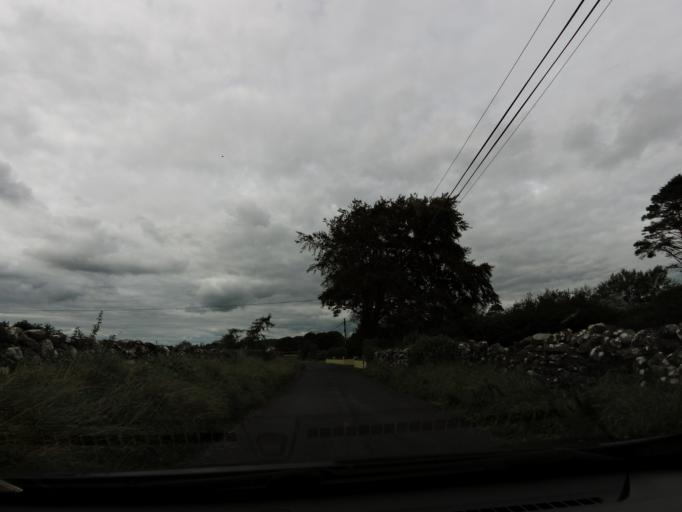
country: IE
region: Connaught
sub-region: County Galway
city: Loughrea
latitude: 53.1490
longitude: -8.4212
